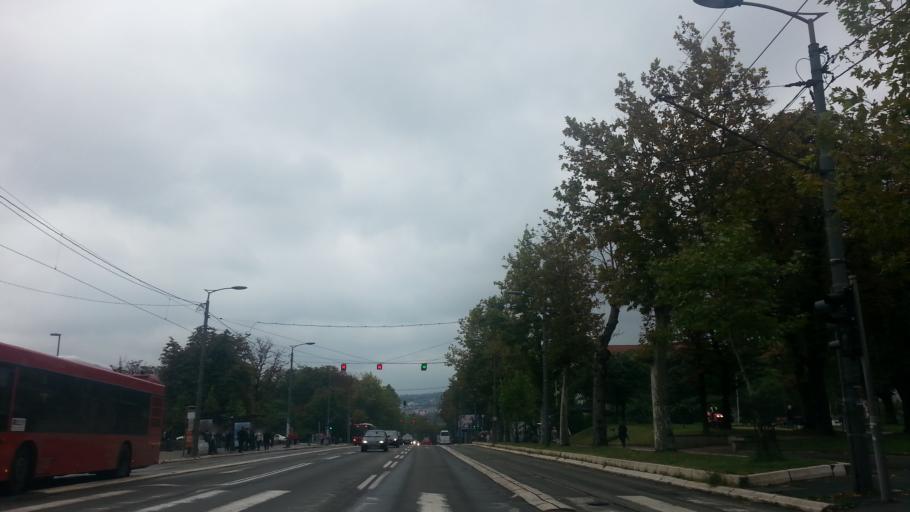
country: RS
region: Central Serbia
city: Belgrade
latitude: 44.7987
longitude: 20.4656
